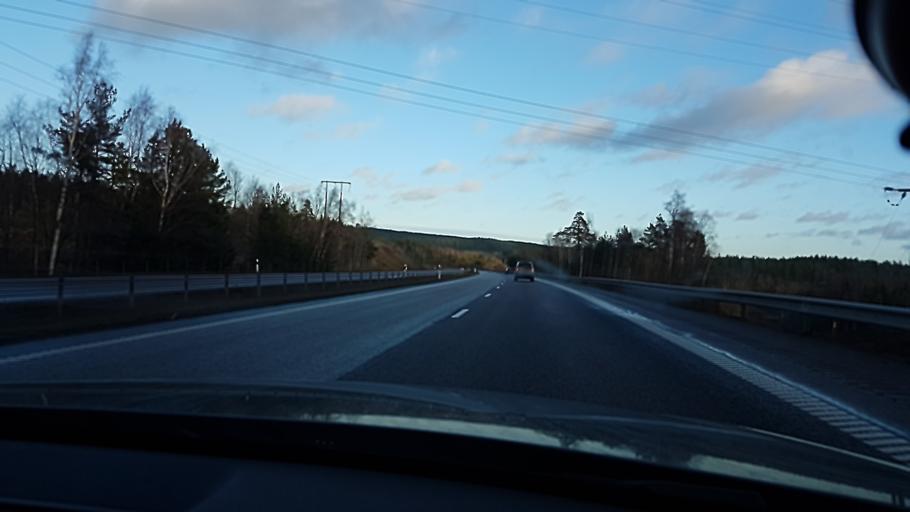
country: SE
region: OEstergoetland
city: Lindo
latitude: 58.6721
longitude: 16.2502
